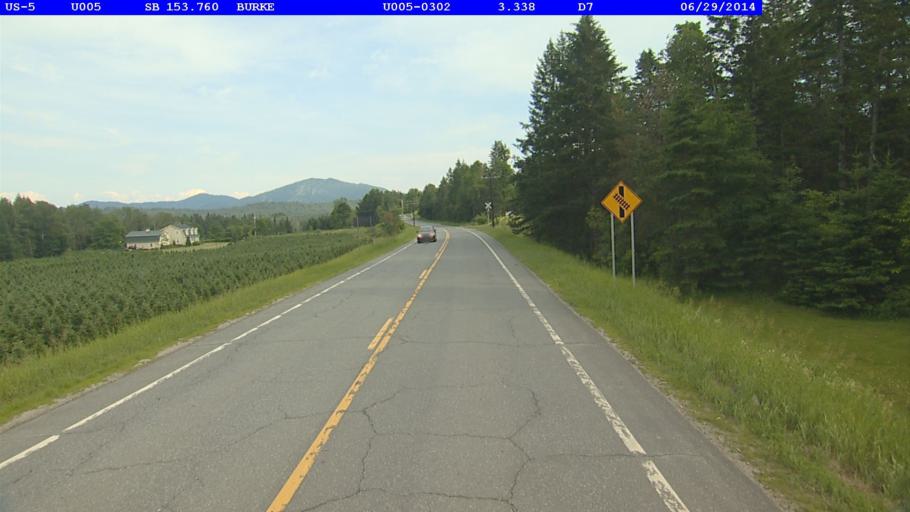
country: US
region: Vermont
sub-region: Caledonia County
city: Lyndonville
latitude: 44.6319
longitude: -71.9738
